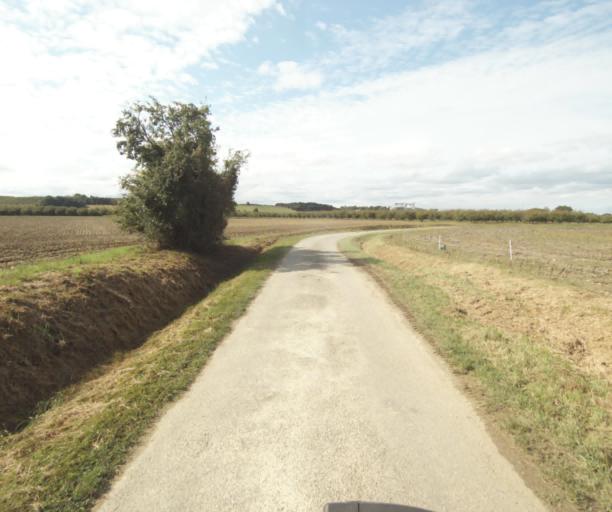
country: FR
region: Midi-Pyrenees
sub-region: Departement du Tarn-et-Garonne
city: Finhan
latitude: 43.8781
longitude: 1.2003
